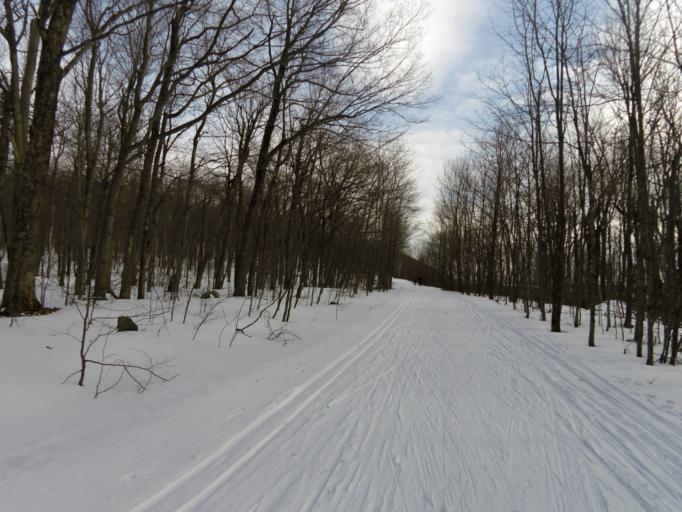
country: CA
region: Quebec
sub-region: Outaouais
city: Wakefield
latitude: 45.5211
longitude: -75.9277
